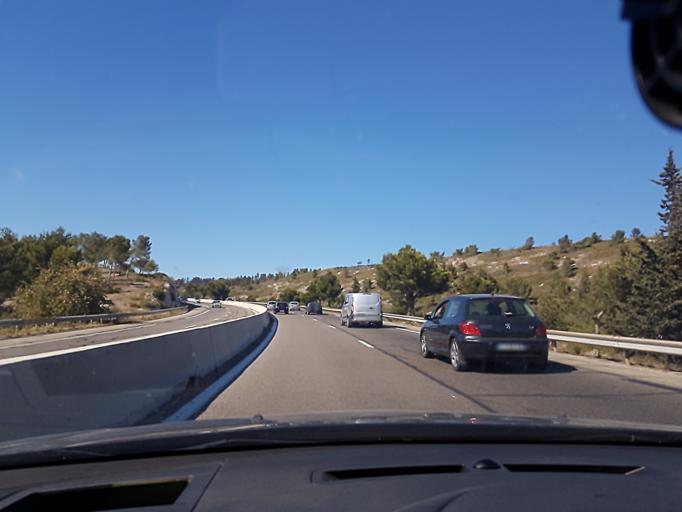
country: FR
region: Provence-Alpes-Cote d'Azur
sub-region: Departement des Bouches-du-Rhone
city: Carry-le-Rouet
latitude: 43.3419
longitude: 5.1692
